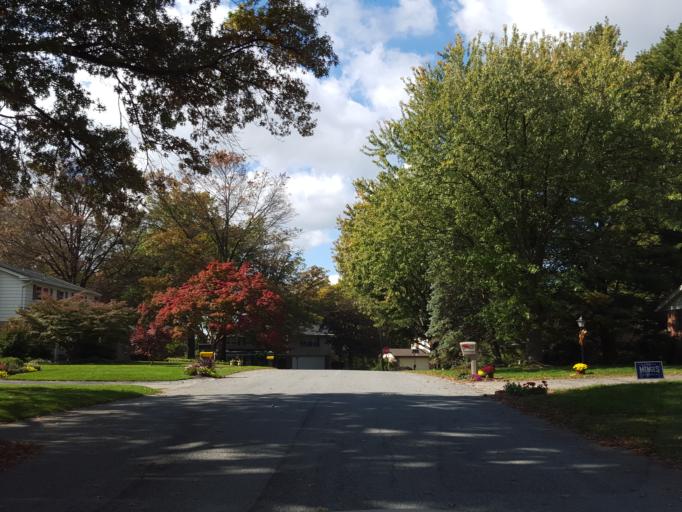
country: US
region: Pennsylvania
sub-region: York County
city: East York
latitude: 39.9657
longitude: -76.6628
